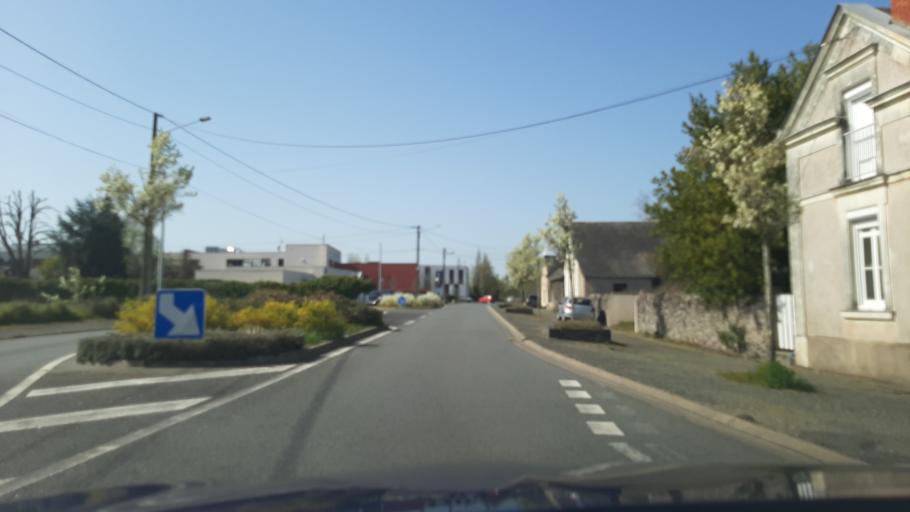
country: FR
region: Pays de la Loire
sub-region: Departement de Maine-et-Loire
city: Les Ponts-de-Ce
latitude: 47.4421
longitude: -0.5226
